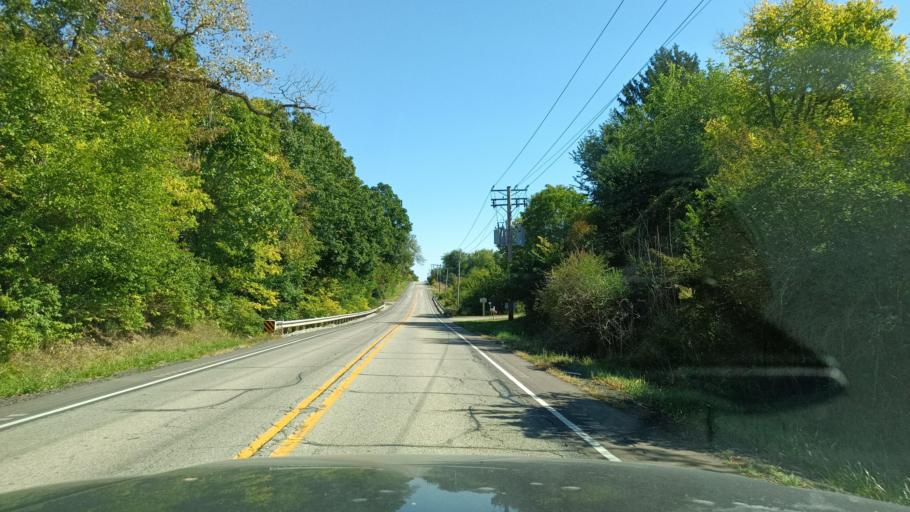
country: US
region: Illinois
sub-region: McLean County
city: Danvers
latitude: 40.6169
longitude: -89.2258
